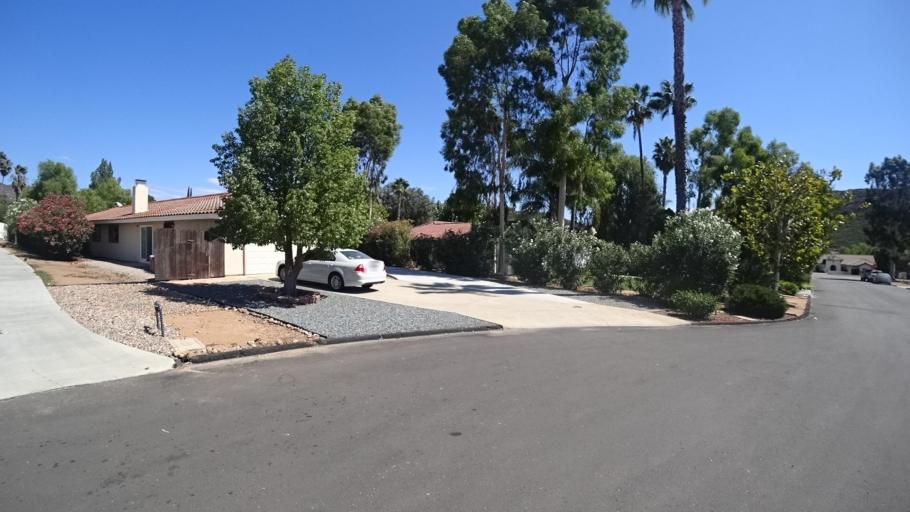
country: US
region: California
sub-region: San Diego County
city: San Diego Country Estates
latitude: 33.0122
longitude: -116.8109
